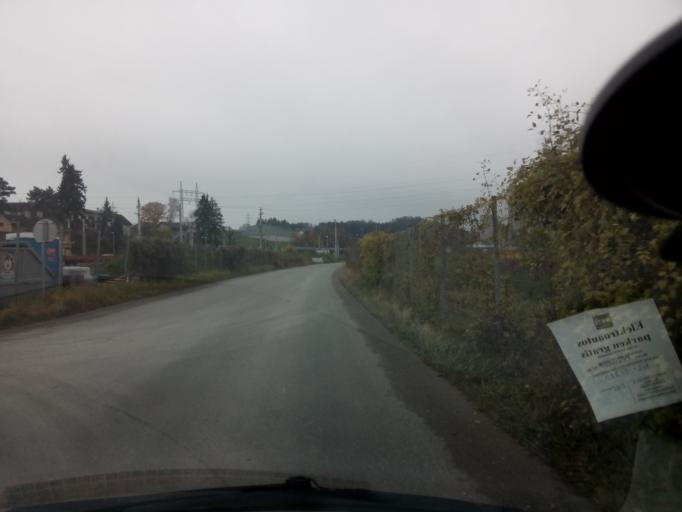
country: AT
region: Upper Austria
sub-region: Politischer Bezirk Gmunden
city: Gmunden
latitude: 47.9276
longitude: 13.7841
